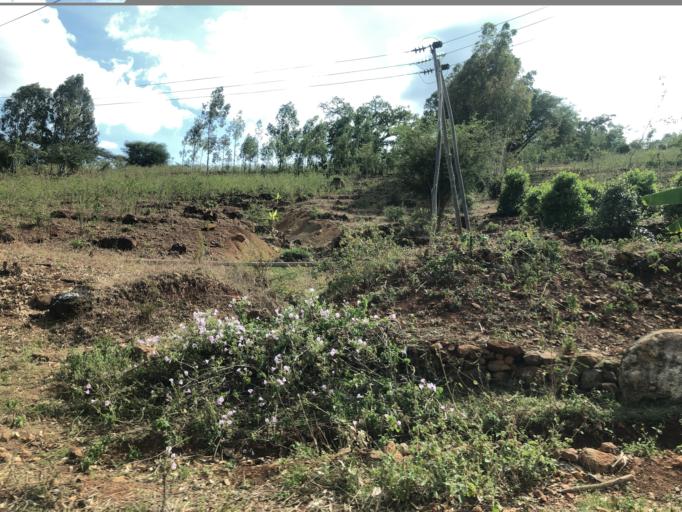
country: ET
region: Southern Nations, Nationalities, and People's Region
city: Konso
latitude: 5.3322
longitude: 37.4305
